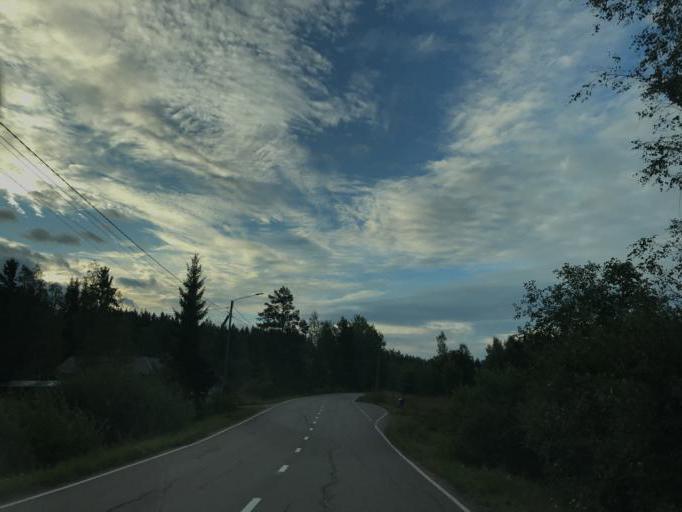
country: FI
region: Uusimaa
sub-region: Helsinki
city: Vihti
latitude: 60.3974
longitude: 24.5074
